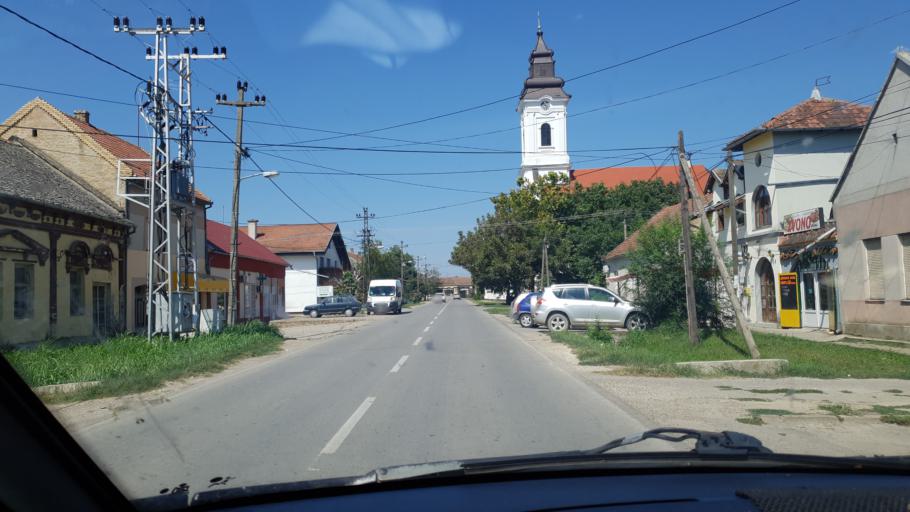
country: RS
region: Autonomna Pokrajina Vojvodina
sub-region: Juznobacki Okrug
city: Kovilj
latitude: 45.2278
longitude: 20.0218
